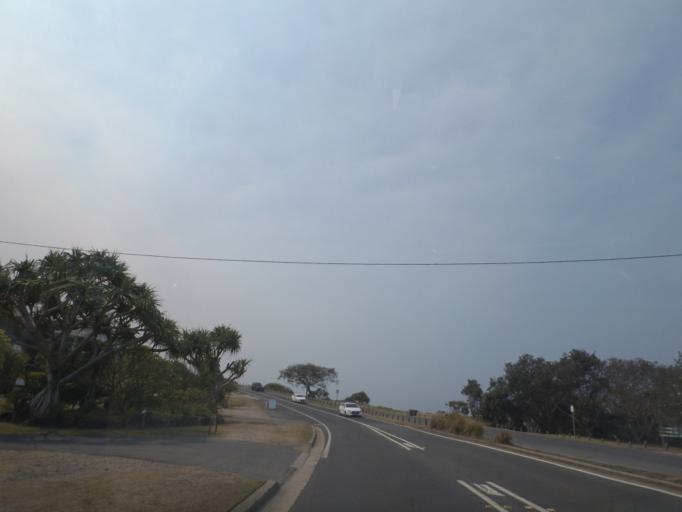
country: AU
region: New South Wales
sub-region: Tweed
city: Casuarina
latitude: -28.3361
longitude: 153.5743
